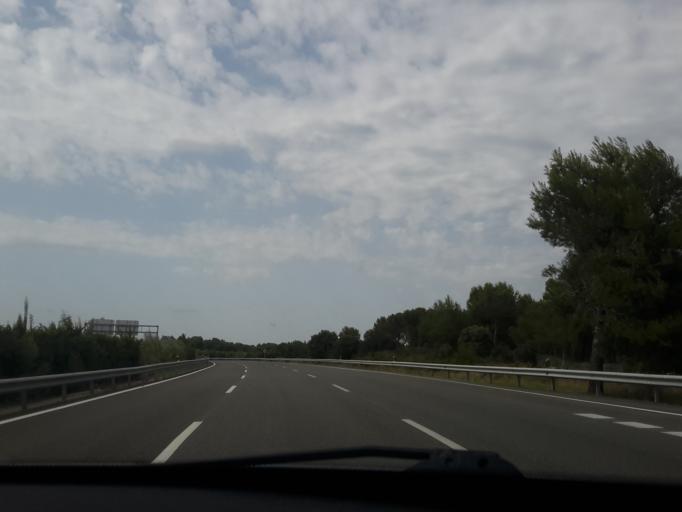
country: ES
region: Catalonia
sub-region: Provincia de Tarragona
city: Montferri
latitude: 41.3021
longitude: 1.3472
